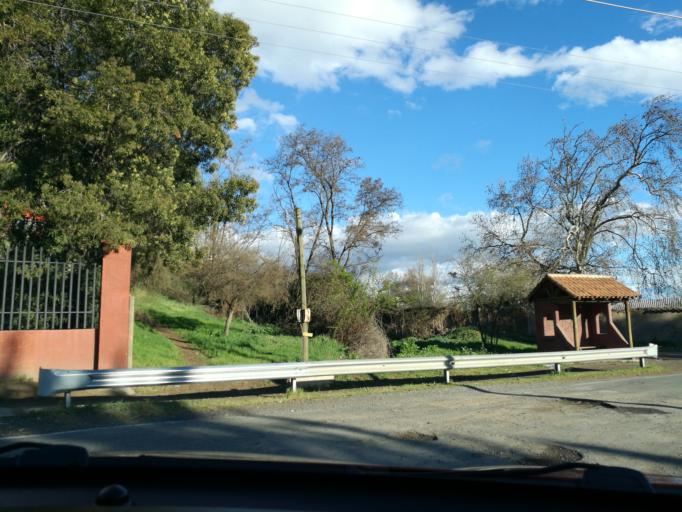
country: CL
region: O'Higgins
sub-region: Provincia de Cachapoal
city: Graneros
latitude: -34.1014
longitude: -70.8094
